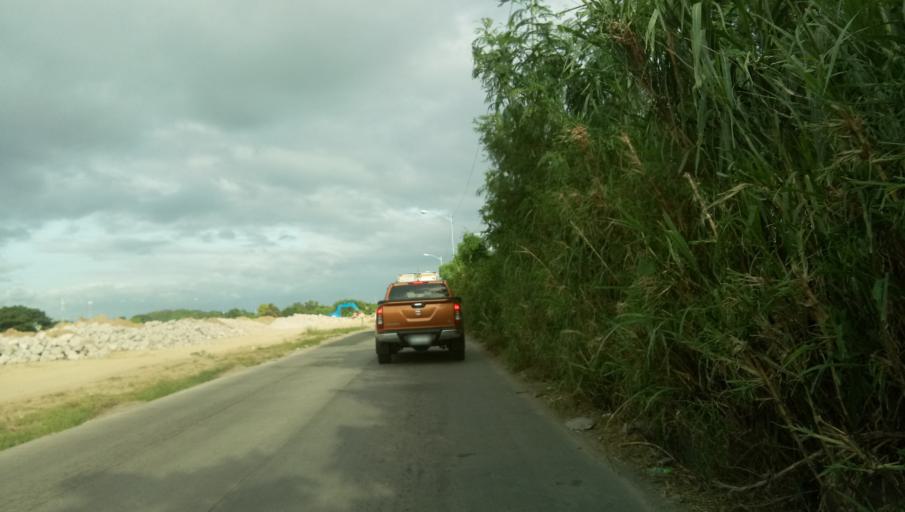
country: PH
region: Calabarzon
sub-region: Province of Cavite
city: Dasmarinas
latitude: 14.3667
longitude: 120.9205
